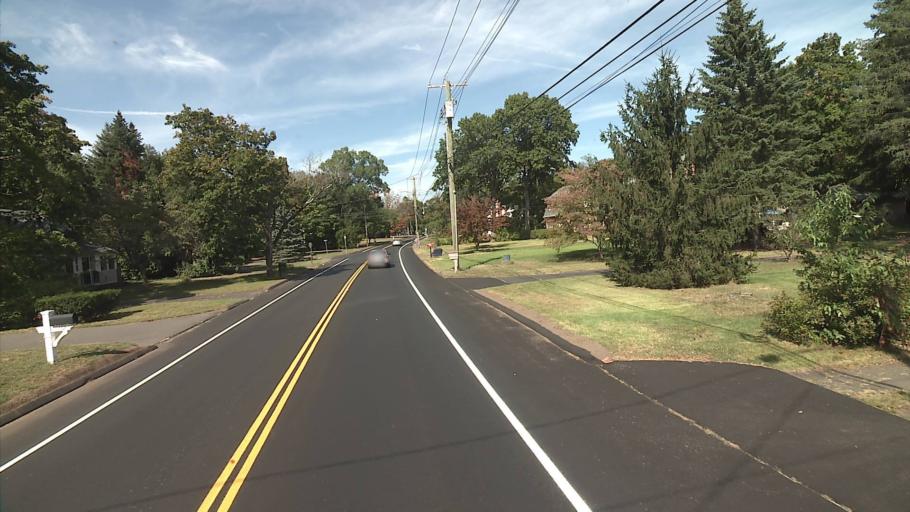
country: US
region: Connecticut
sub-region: New Haven County
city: North Haven
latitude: 41.3794
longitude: -72.8572
